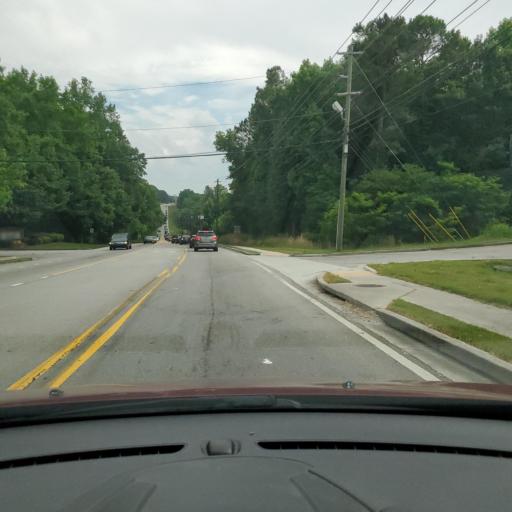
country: US
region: Georgia
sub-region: Henry County
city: Stockbridge
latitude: 33.5235
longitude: -84.2306
